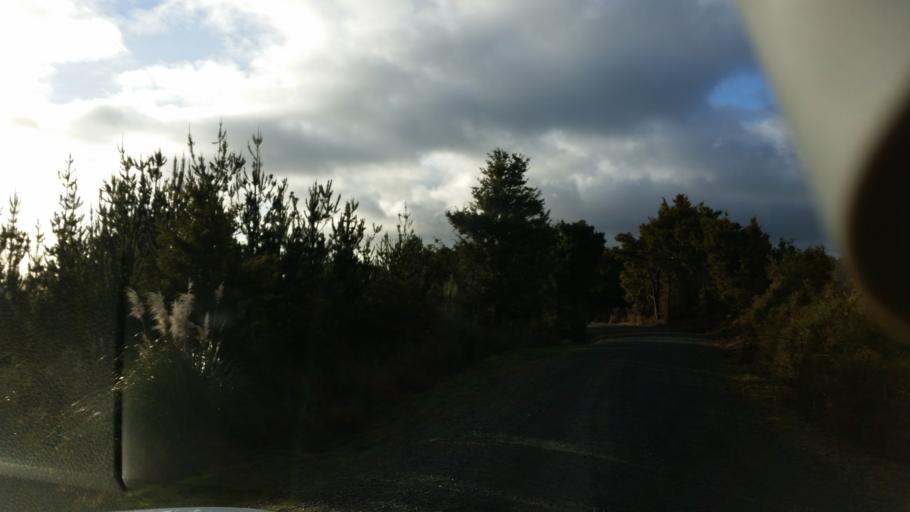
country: NZ
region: Northland
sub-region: Whangarei
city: Maungatapere
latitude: -35.7853
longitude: 174.0831
